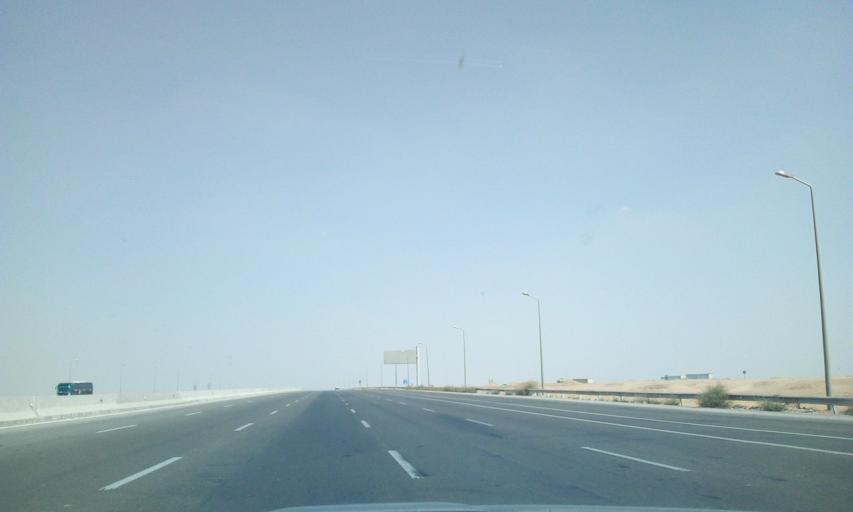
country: EG
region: Muhafazat al Qahirah
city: Halwan
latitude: 29.9055
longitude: 31.7032
